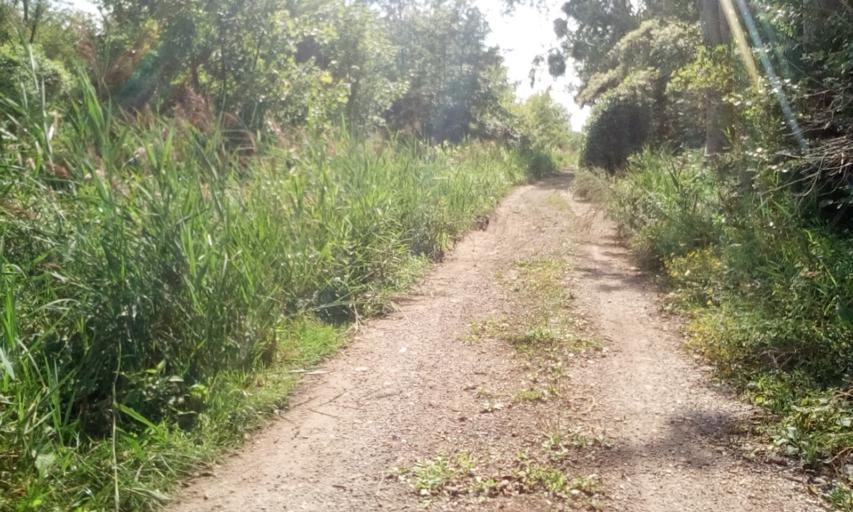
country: FR
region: Lower Normandy
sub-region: Departement du Calvados
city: Argences
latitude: 49.1469
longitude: -0.1798
